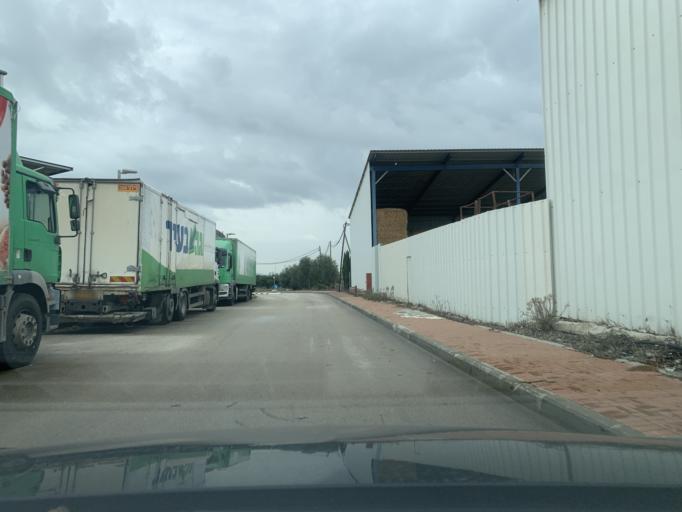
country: PS
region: West Bank
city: Qalqilyah
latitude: 32.2085
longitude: 34.9792
